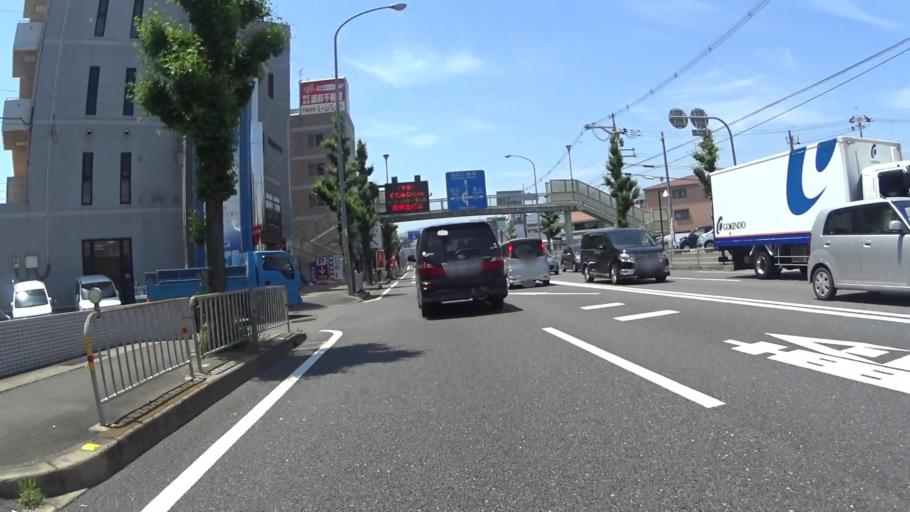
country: JP
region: Kyoto
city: Muko
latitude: 34.9844
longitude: 135.6954
